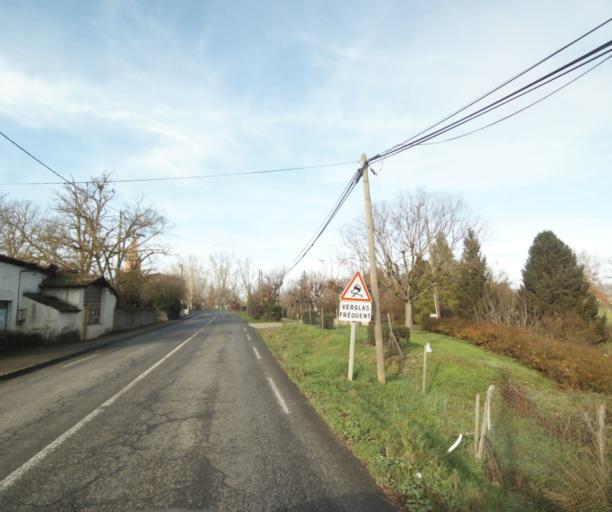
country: FR
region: Midi-Pyrenees
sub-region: Departement de la Haute-Garonne
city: Villemur-sur-Tarn
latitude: 43.8609
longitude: 1.4816
